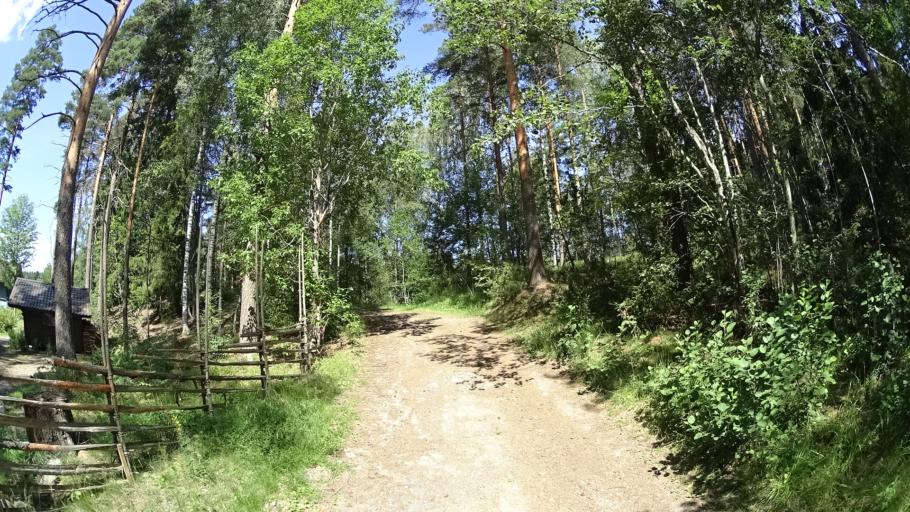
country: FI
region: Haeme
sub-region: Forssa
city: Tammela
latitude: 60.7694
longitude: 23.8707
